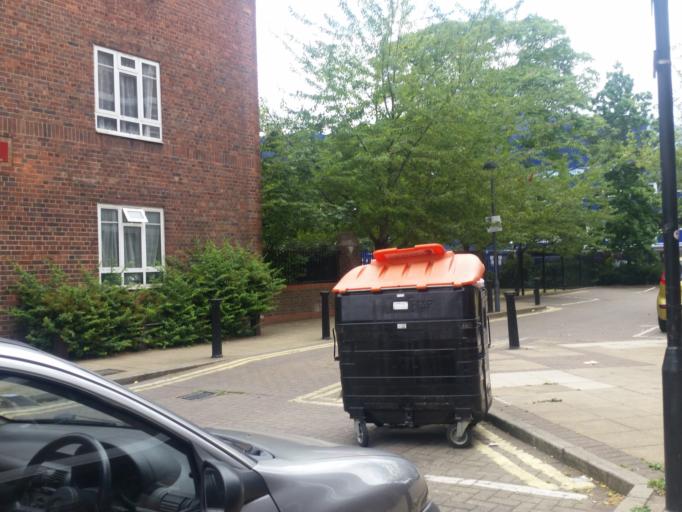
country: GB
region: England
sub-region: Greater London
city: Hammersmith
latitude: 51.5105
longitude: -0.2334
